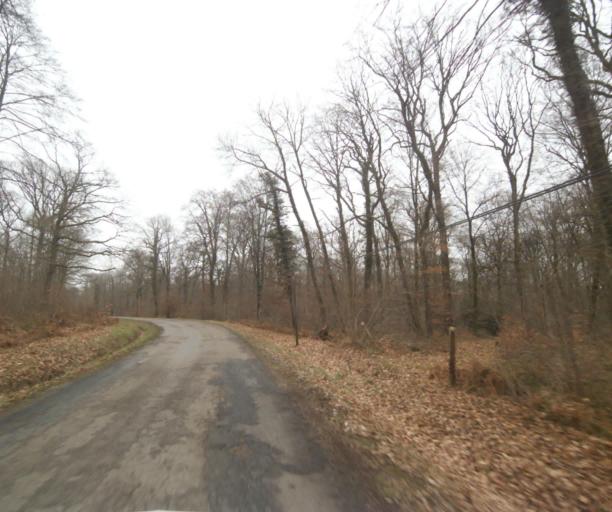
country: FR
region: Champagne-Ardenne
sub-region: Departement de la Haute-Marne
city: Wassy
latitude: 48.5213
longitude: 4.9740
